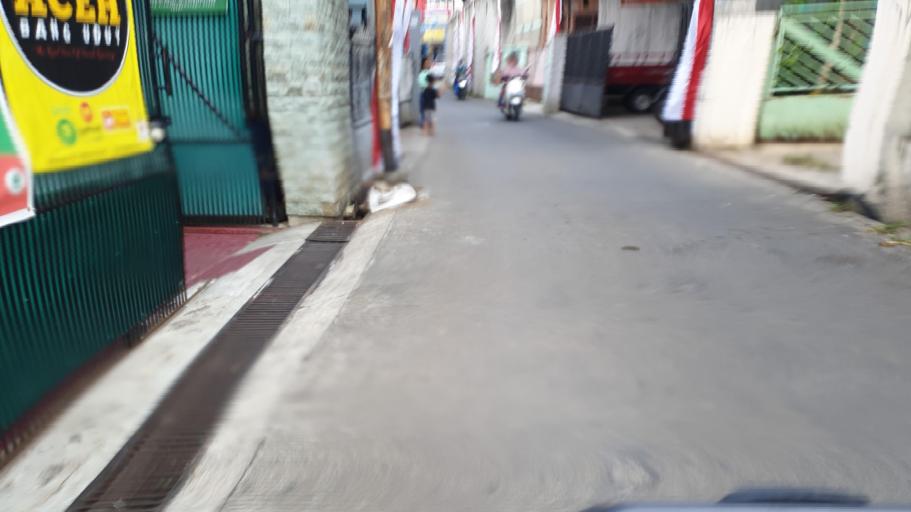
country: ID
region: West Java
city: Depok
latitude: -6.3718
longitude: 106.8515
